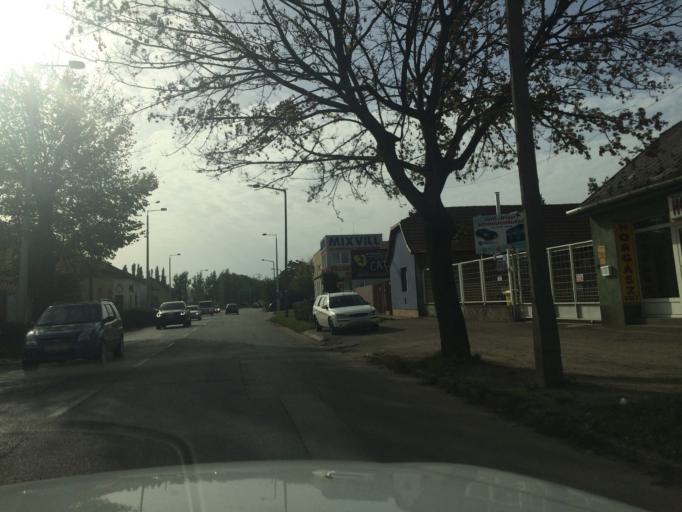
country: HU
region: Szabolcs-Szatmar-Bereg
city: Nyiregyhaza
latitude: 47.9447
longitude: 21.7195
